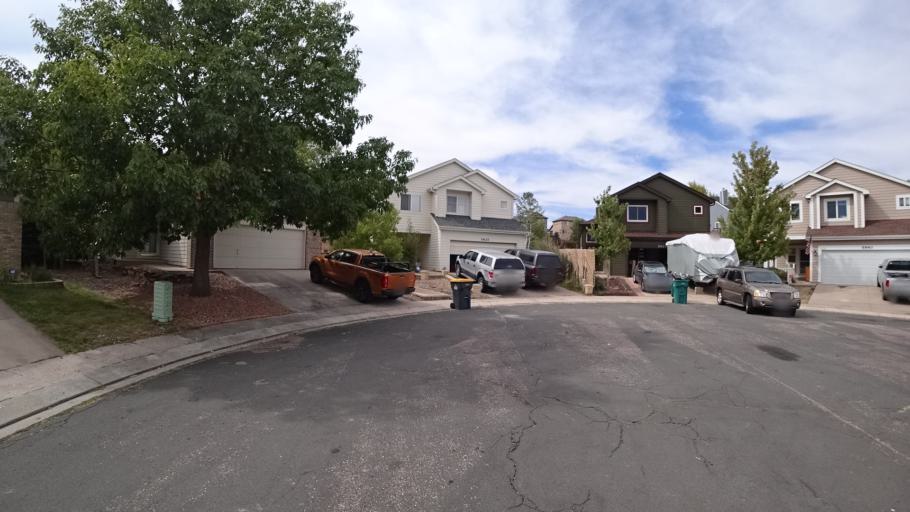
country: US
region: Colorado
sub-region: El Paso County
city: Cimarron Hills
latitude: 38.9089
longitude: -104.7060
